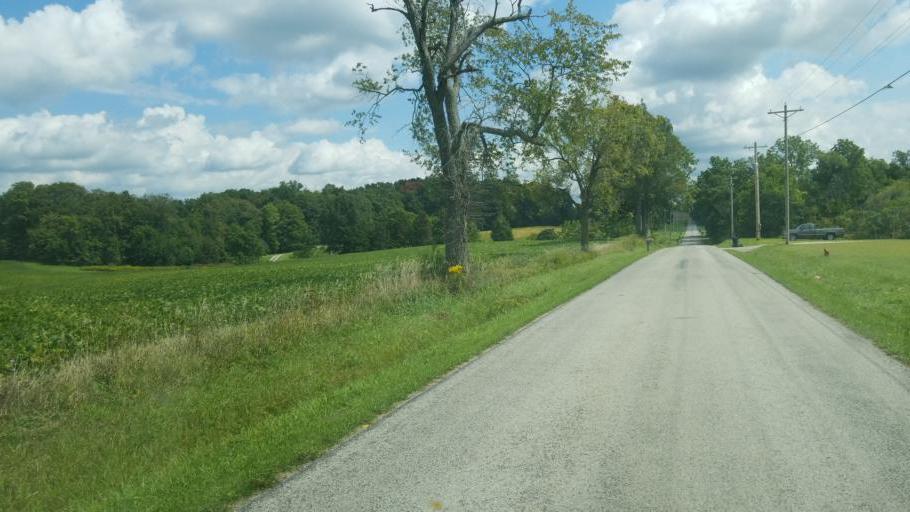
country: US
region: Ohio
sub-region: Huron County
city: Monroeville
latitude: 41.1648
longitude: -82.6792
